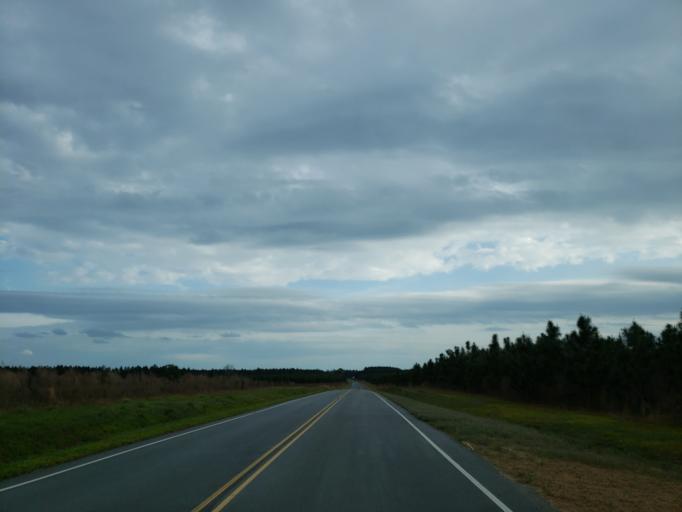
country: US
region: Georgia
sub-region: Dooly County
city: Vienna
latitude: 32.1159
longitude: -83.7560
